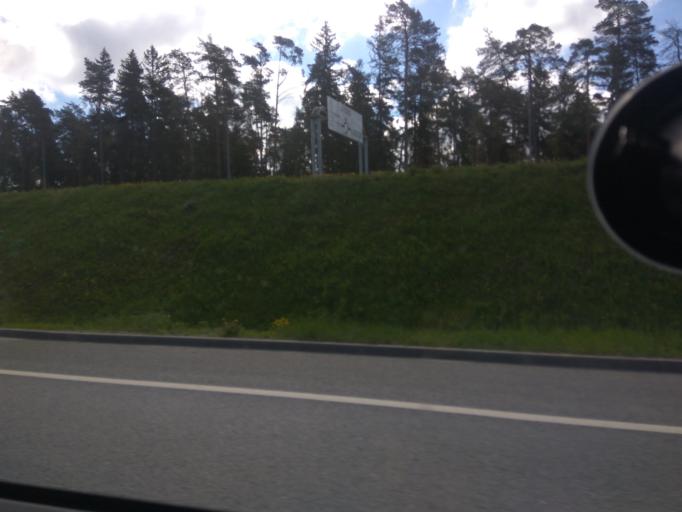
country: RU
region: Moskovskaya
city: Zhukovskiy
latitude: 55.5791
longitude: 38.1214
